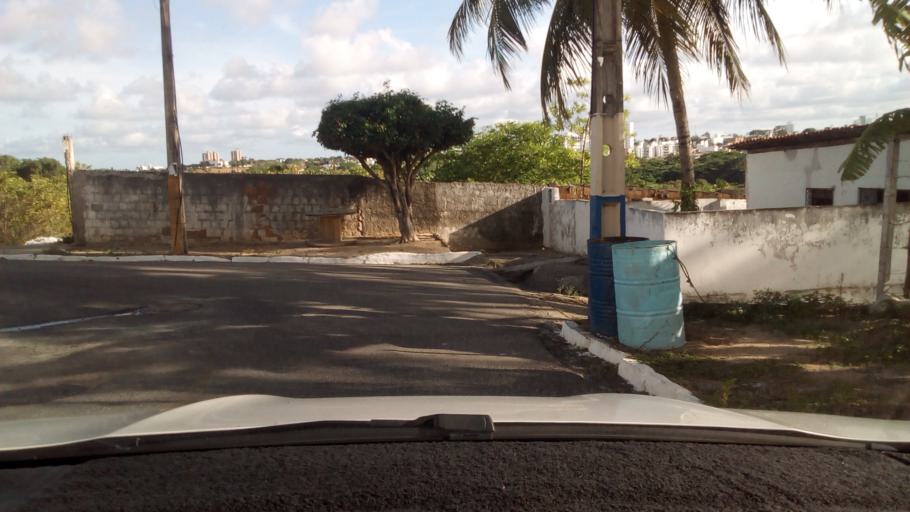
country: BR
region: Paraiba
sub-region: Joao Pessoa
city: Joao Pessoa
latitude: -7.1373
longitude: -34.8338
